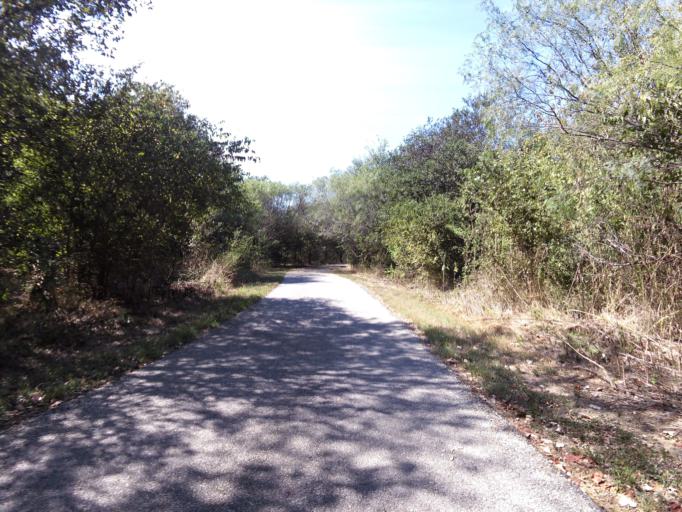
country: US
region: Texas
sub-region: Bexar County
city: China Grove
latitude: 29.3902
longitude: -98.4208
